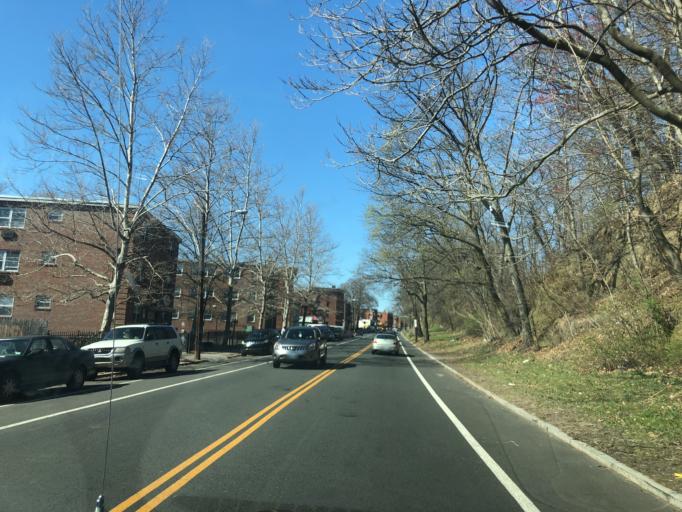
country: US
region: Connecticut
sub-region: Hartford County
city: Hartford
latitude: 41.7517
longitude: -72.6936
